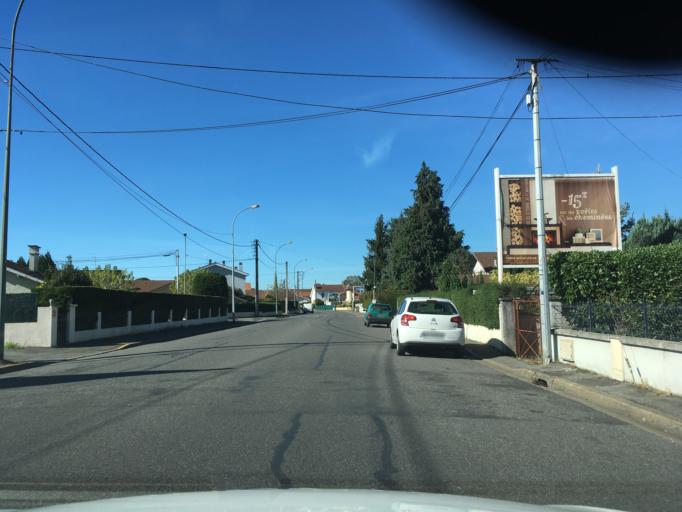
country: FR
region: Aquitaine
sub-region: Departement des Pyrenees-Atlantiques
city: Pau
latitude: 43.3240
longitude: -0.3750
